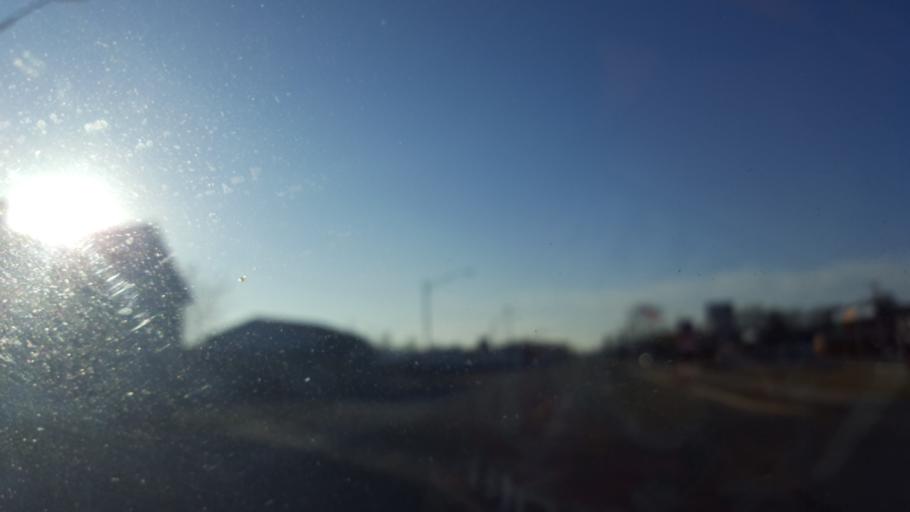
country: US
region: Indiana
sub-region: Elkhart County
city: Nappanee
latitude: 41.4427
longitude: -86.0121
